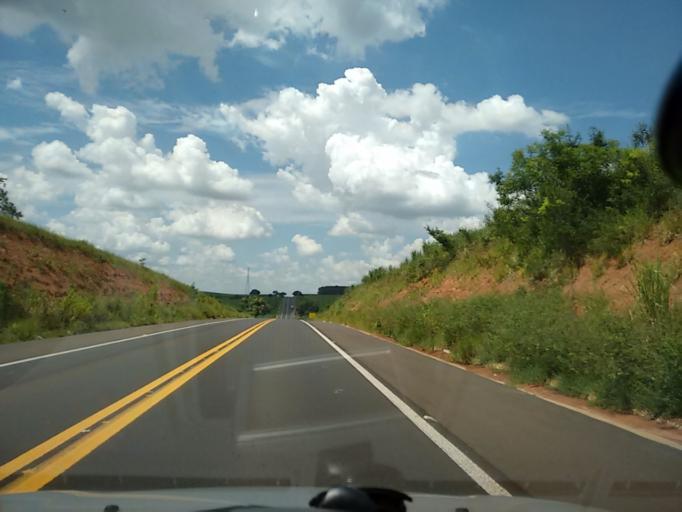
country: BR
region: Sao Paulo
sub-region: Osvaldo Cruz
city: Osvaldo Cruz
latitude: -21.8718
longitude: -50.8560
